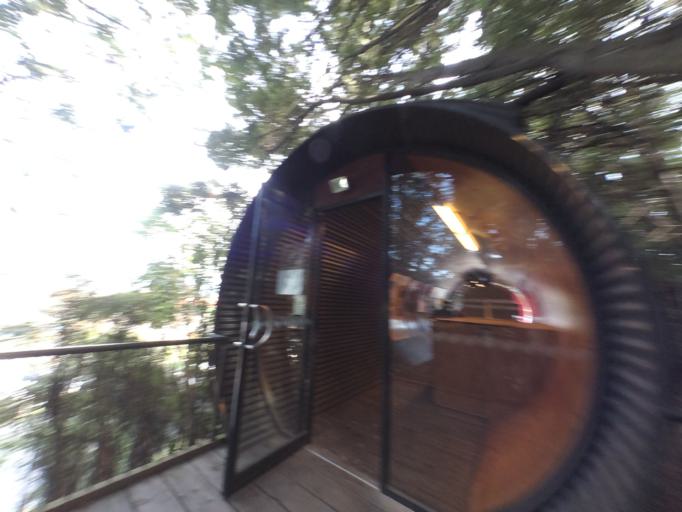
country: NZ
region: Otago
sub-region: Queenstown-Lakes District
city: Queenstown
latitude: -45.0288
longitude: 168.6565
